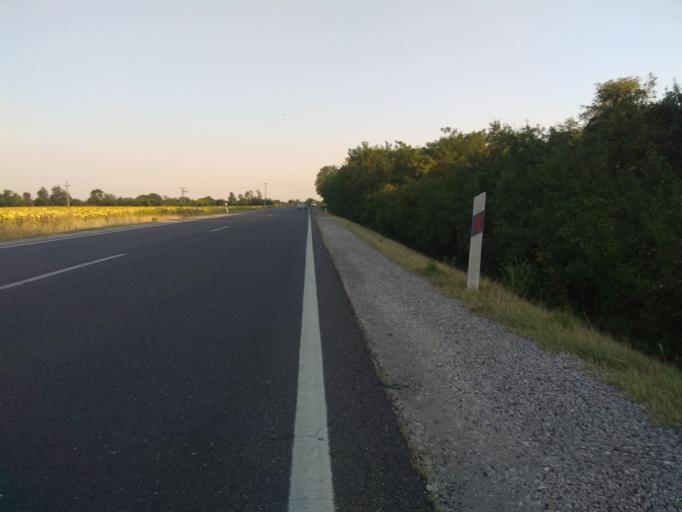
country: HU
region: Borsod-Abauj-Zemplen
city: Nyekladhaza
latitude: 47.9680
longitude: 20.8320
